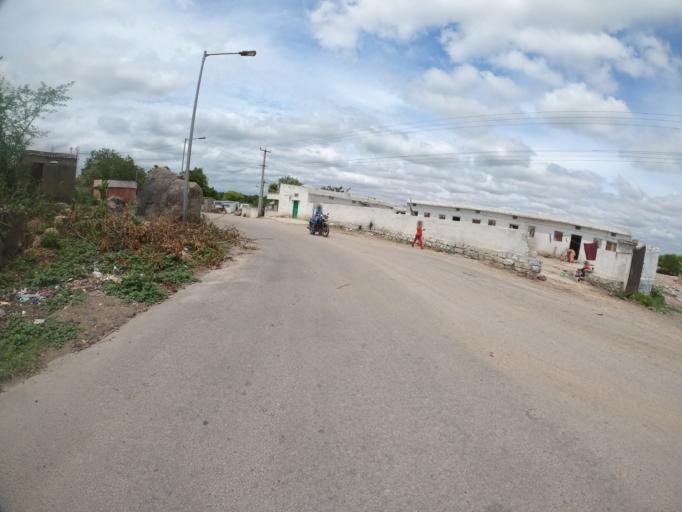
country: IN
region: Telangana
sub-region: Hyderabad
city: Hyderabad
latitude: 17.2990
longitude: 78.3784
